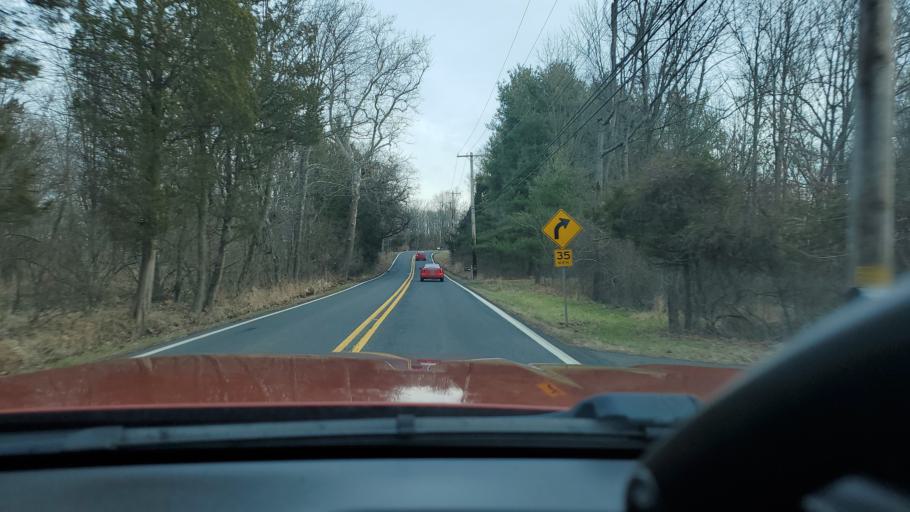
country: US
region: Pennsylvania
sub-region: Montgomery County
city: Woxall
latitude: 40.3326
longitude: -75.4102
